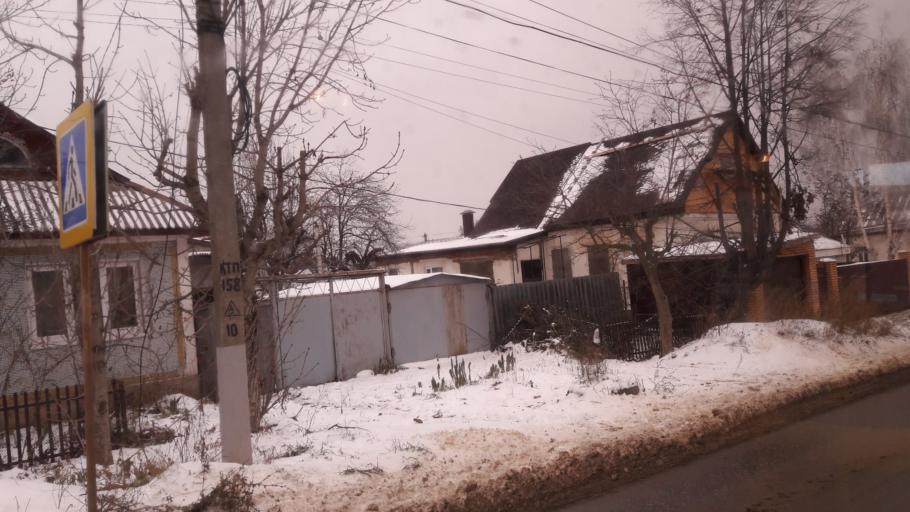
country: RU
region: Tula
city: Gorelki
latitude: 54.2337
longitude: 37.6363
